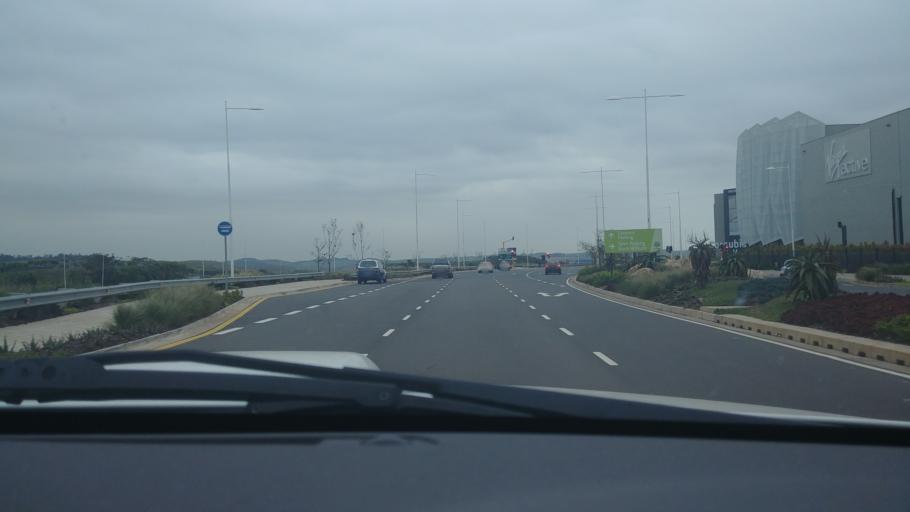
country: ZA
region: KwaZulu-Natal
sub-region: eThekwini Metropolitan Municipality
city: Durban
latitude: -29.7107
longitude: 31.0525
